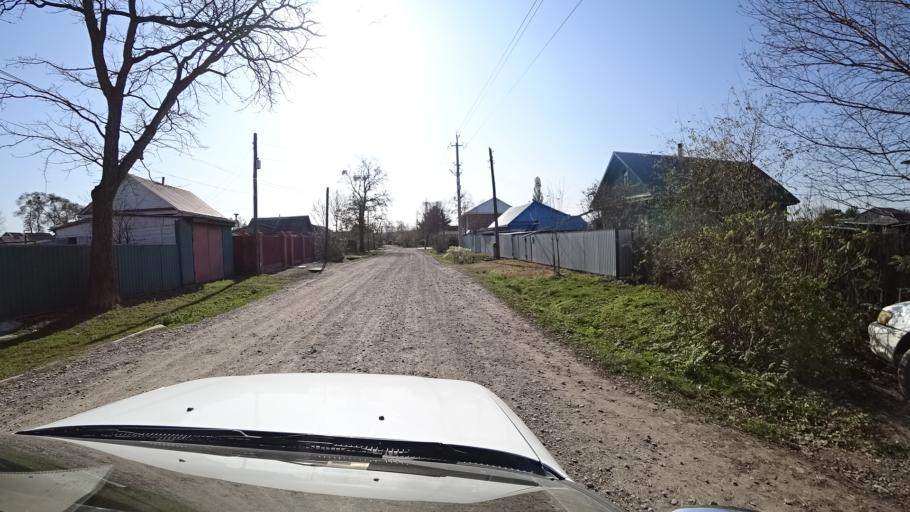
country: RU
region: Primorskiy
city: Dal'nerechensk
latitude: 45.9265
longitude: 133.7206
